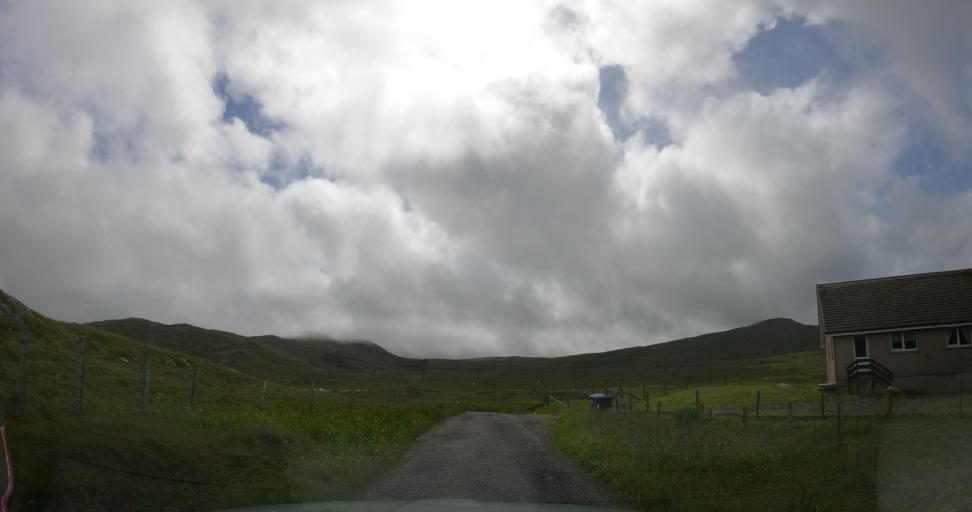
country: GB
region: Scotland
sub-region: Eilean Siar
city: Barra
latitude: 57.0024
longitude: -7.4801
